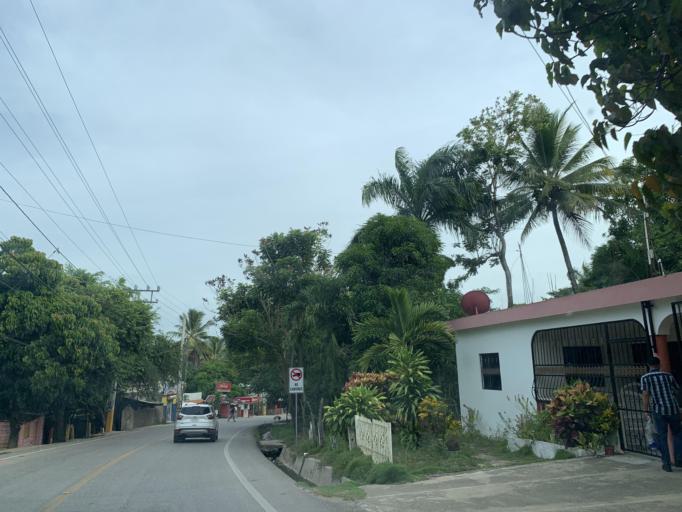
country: DO
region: Puerto Plata
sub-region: Puerto Plata
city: Puerto Plata
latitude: 19.7196
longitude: -70.6196
